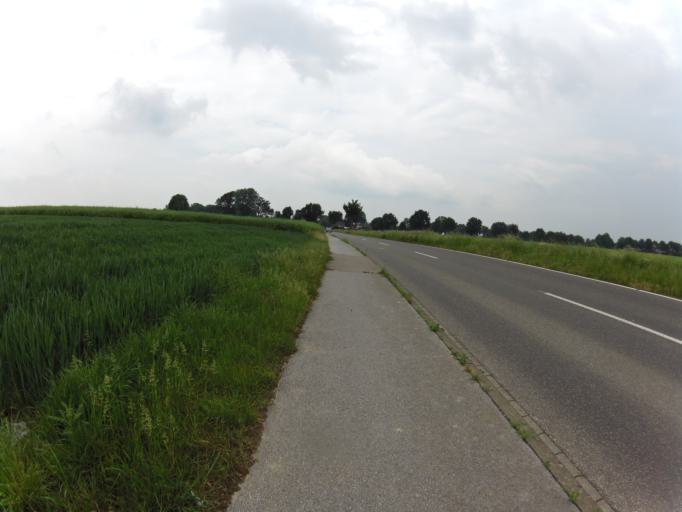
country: DE
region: North Rhine-Westphalia
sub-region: Regierungsbezirk Koln
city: Ubach-Palenberg
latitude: 50.9405
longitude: 6.1584
